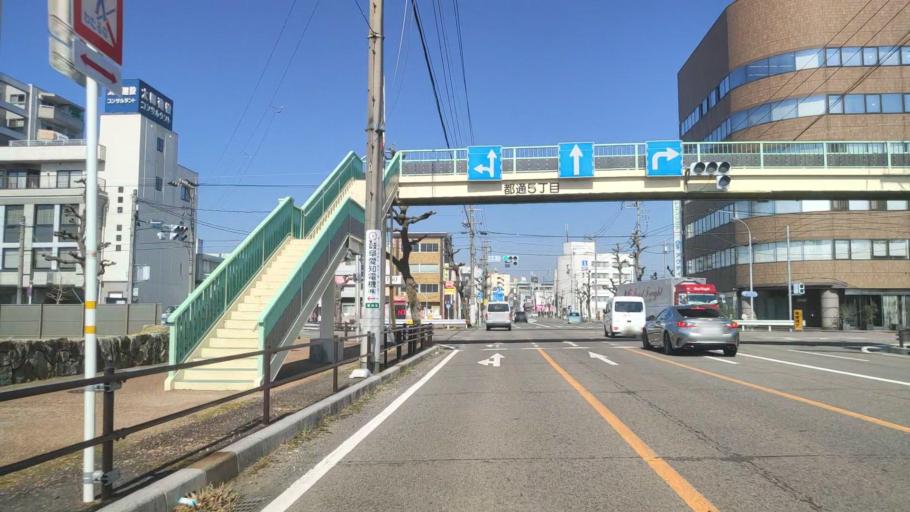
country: JP
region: Gifu
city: Gifu-shi
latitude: 35.4147
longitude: 136.7471
